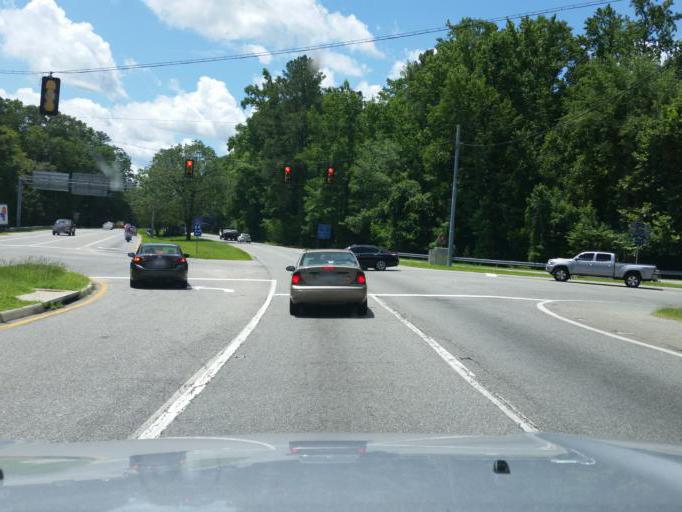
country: US
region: Virginia
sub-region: City of Williamsburg
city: Williamsburg
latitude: 37.3024
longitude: -76.6849
